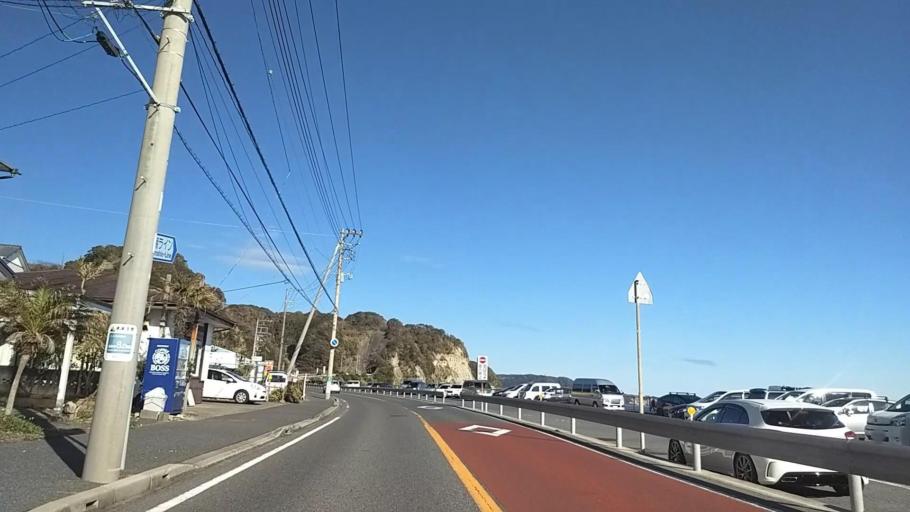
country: JP
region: Chiba
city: Katsuura
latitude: 35.1684
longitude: 140.3365
